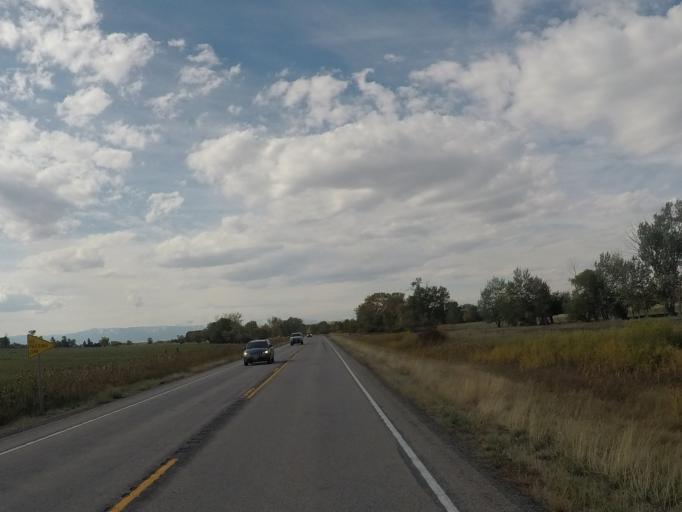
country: US
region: Montana
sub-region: Stillwater County
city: Columbus
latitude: 45.4563
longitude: -109.0703
